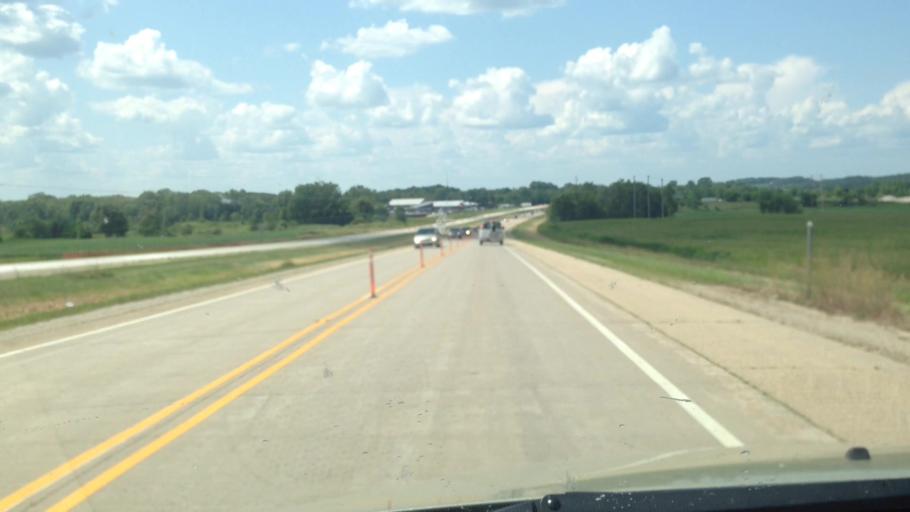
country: US
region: Wisconsin
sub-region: Shawano County
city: Bonduel
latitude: 44.7015
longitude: -88.3646
